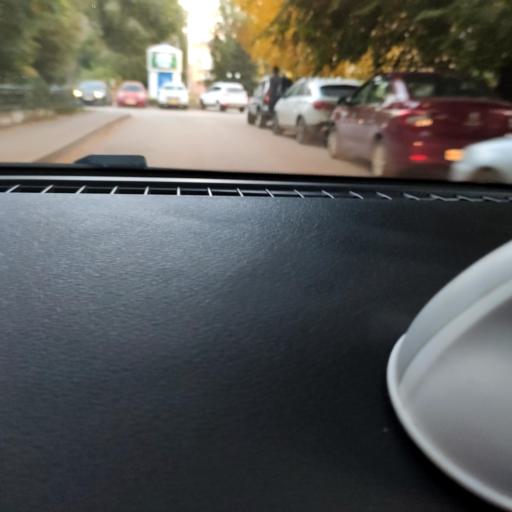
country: RU
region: Samara
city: Samara
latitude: 53.2357
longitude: 50.2185
